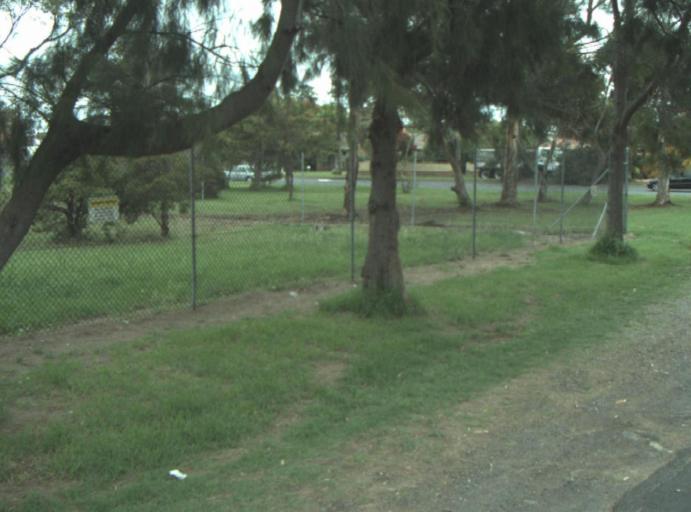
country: AU
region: Victoria
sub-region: Greater Geelong
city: East Geelong
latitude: -38.1553
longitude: 144.3837
